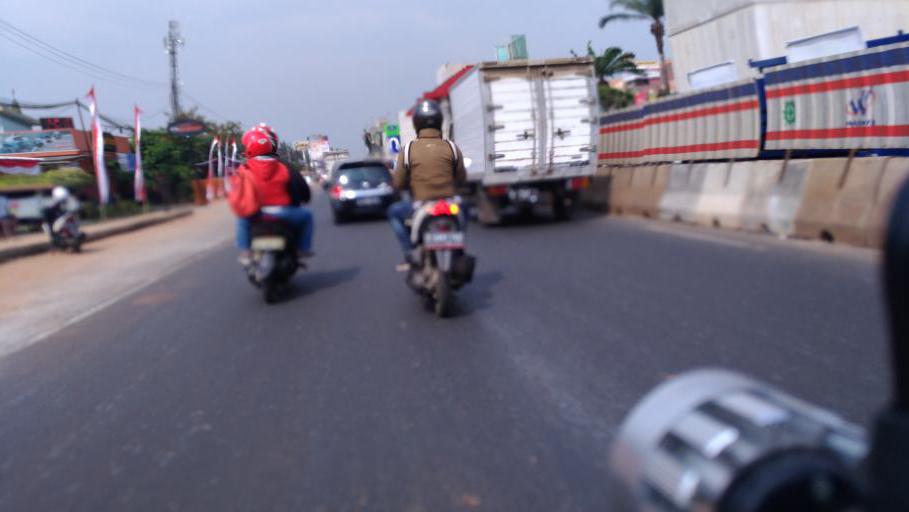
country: ID
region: West Java
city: Cileungsir
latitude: -6.3821
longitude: 106.9281
